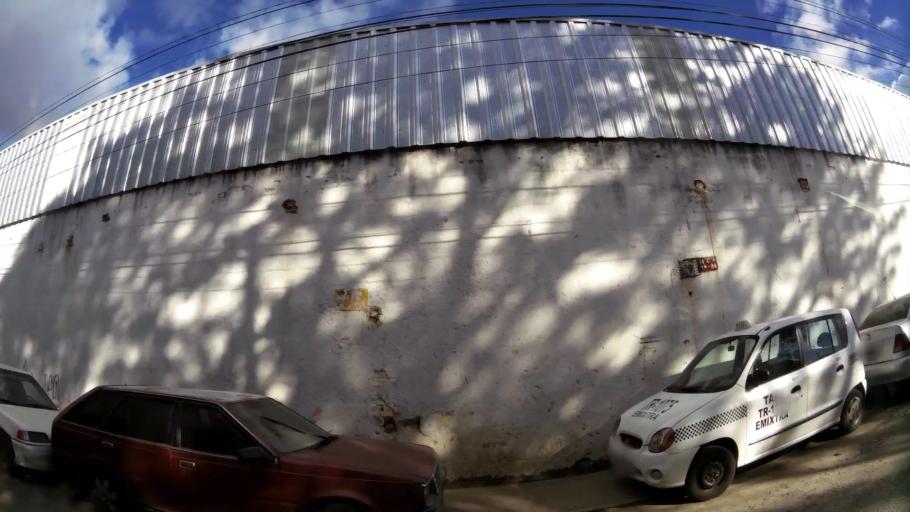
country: GT
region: Guatemala
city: Guatemala City
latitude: 14.6325
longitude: -90.5008
